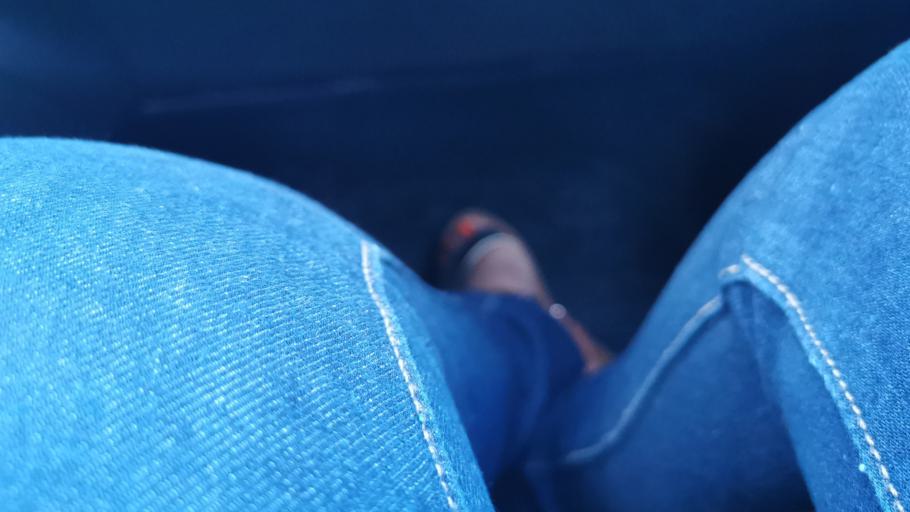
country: NI
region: Atlantico Sur
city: Laguna de Perlas
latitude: 12.2490
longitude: -83.7447
